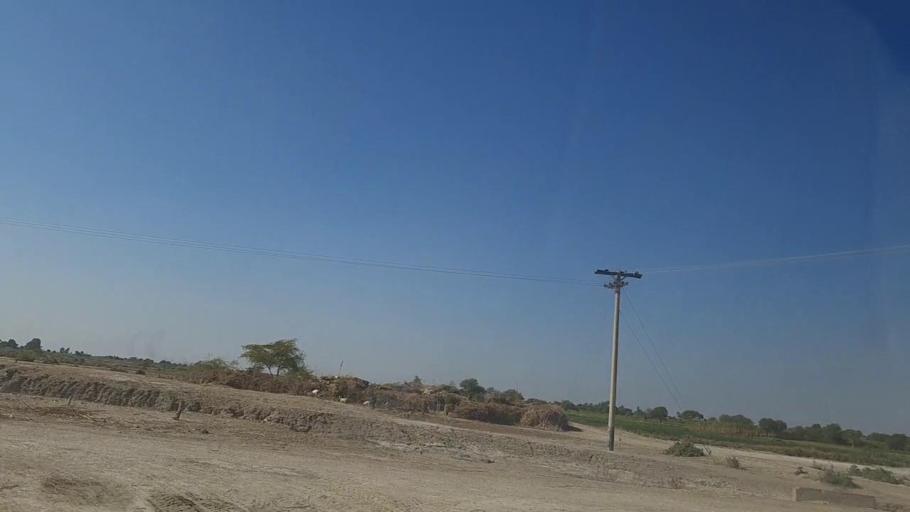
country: PK
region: Sindh
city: Digri
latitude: 25.1309
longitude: 69.0594
